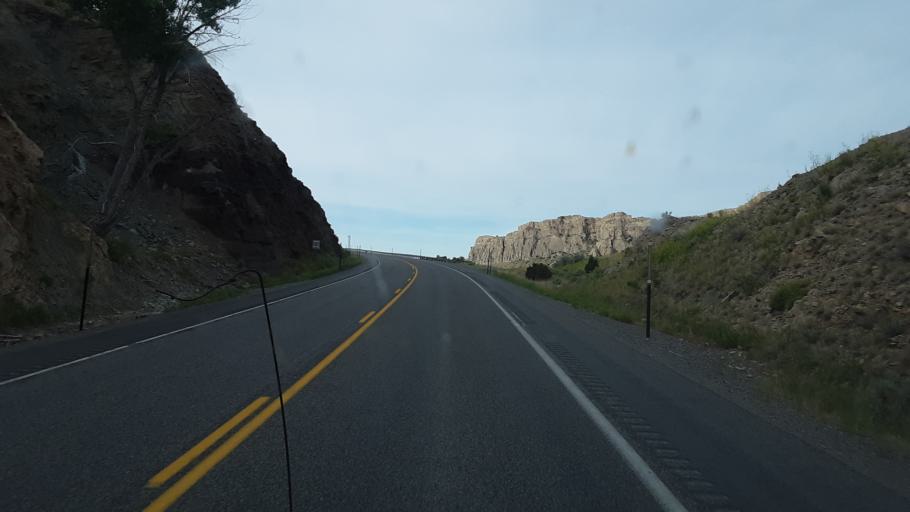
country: US
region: Wyoming
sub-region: Hot Springs County
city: Thermopolis
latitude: 43.4242
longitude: -108.1768
